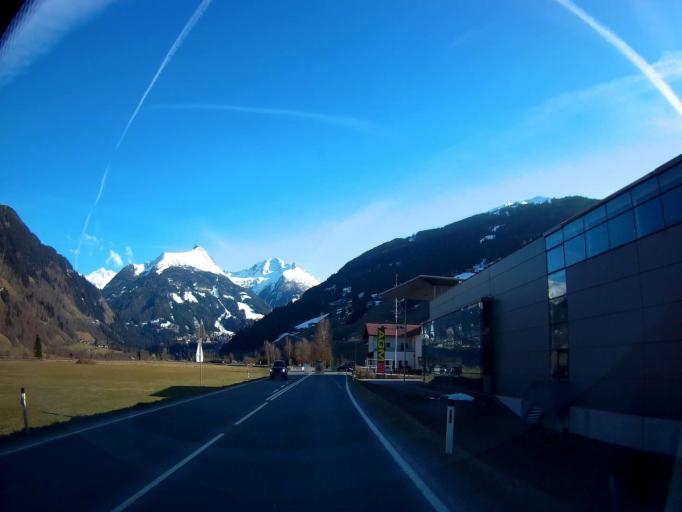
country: AT
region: Salzburg
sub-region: Politischer Bezirk Sankt Johann im Pongau
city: Bad Hofgastein
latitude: 47.1503
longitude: 13.1134
